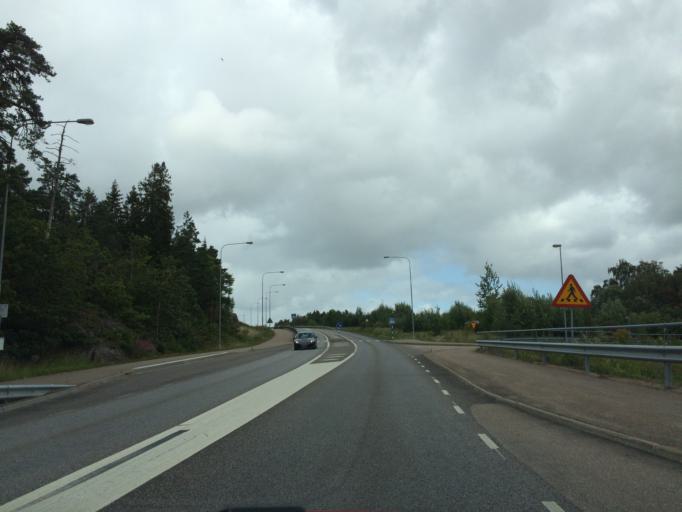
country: SE
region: Vaestra Goetaland
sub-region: Trollhattan
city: Trollhattan
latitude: 58.2924
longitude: 12.2863
